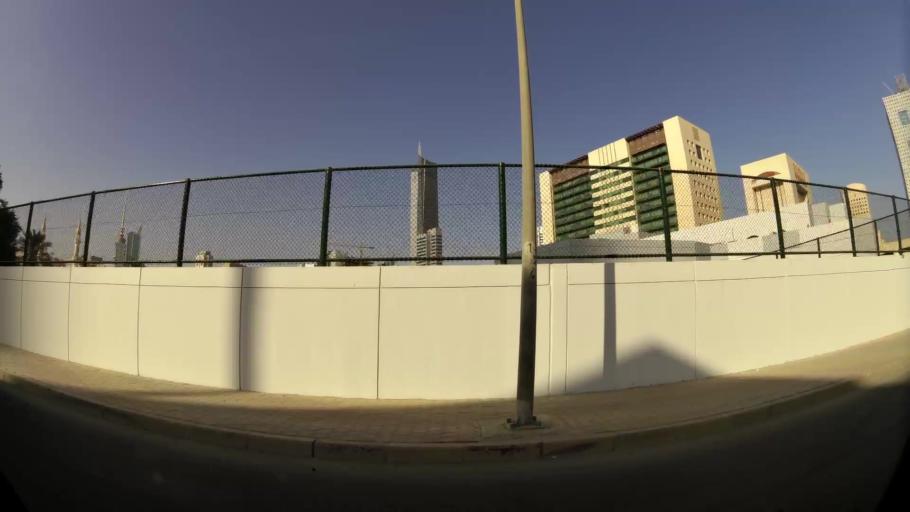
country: KW
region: Al Asimah
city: Kuwait City
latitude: 29.3782
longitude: 47.9836
